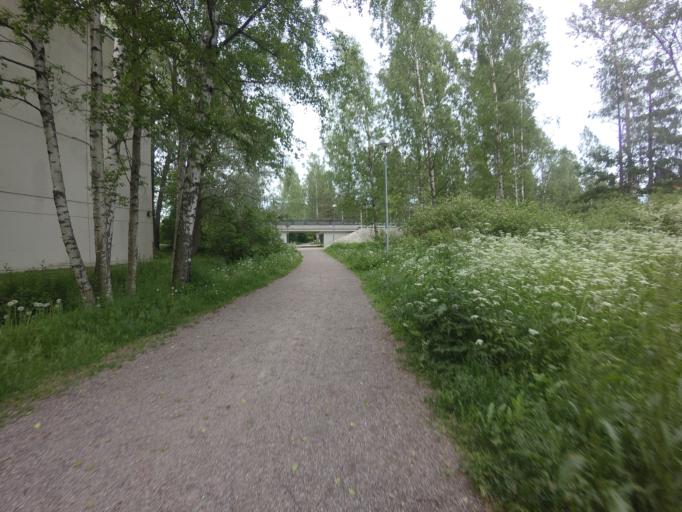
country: FI
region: Uusimaa
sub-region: Helsinki
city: Koukkuniemi
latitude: 60.1526
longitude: 24.7470
